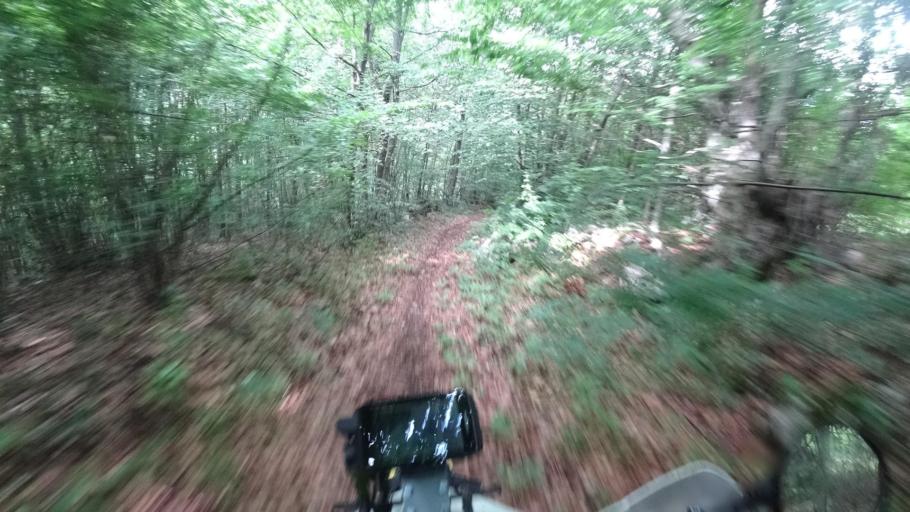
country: HR
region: Licko-Senjska
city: Jezerce
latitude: 44.9226
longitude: 15.6224
